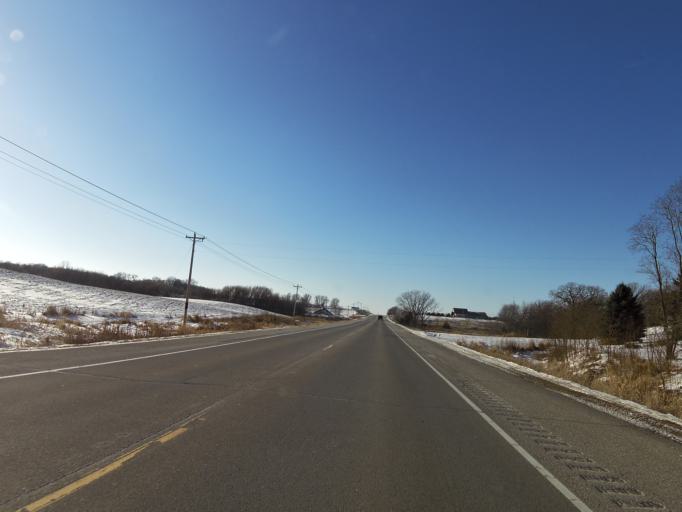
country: US
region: Minnesota
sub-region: Le Sueur County
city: New Prague
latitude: 44.5437
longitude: -93.5128
